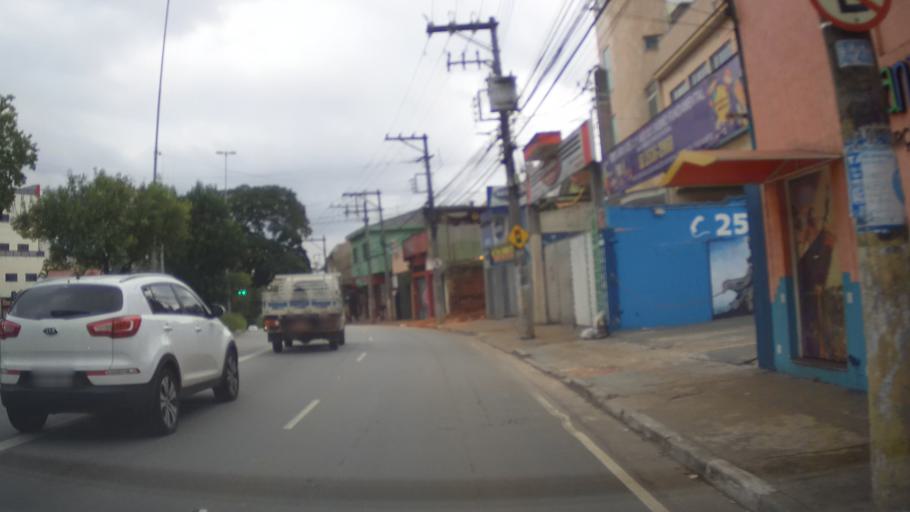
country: BR
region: Sao Paulo
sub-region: Guarulhos
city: Guarulhos
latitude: -23.4668
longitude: -46.5465
